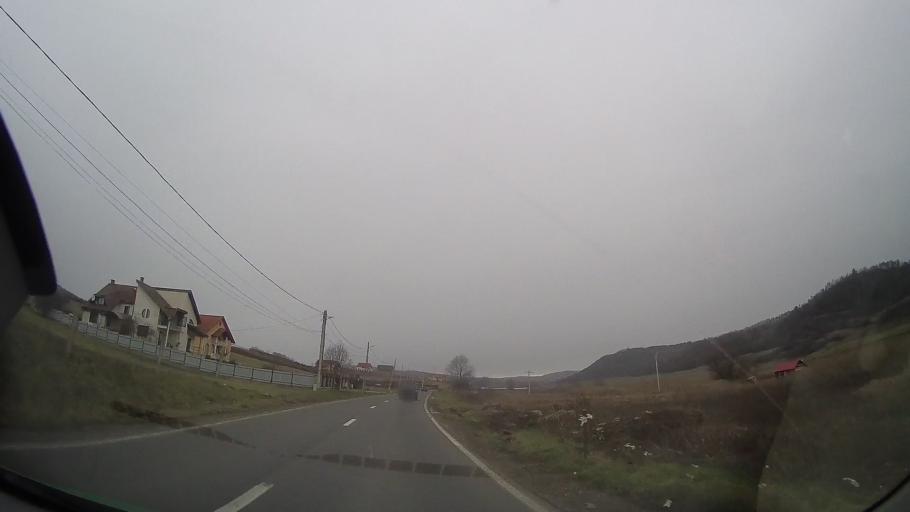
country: RO
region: Mures
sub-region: Comuna Ceausu de Campie
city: Ceausu de Campie
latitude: 46.6225
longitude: 24.5230
